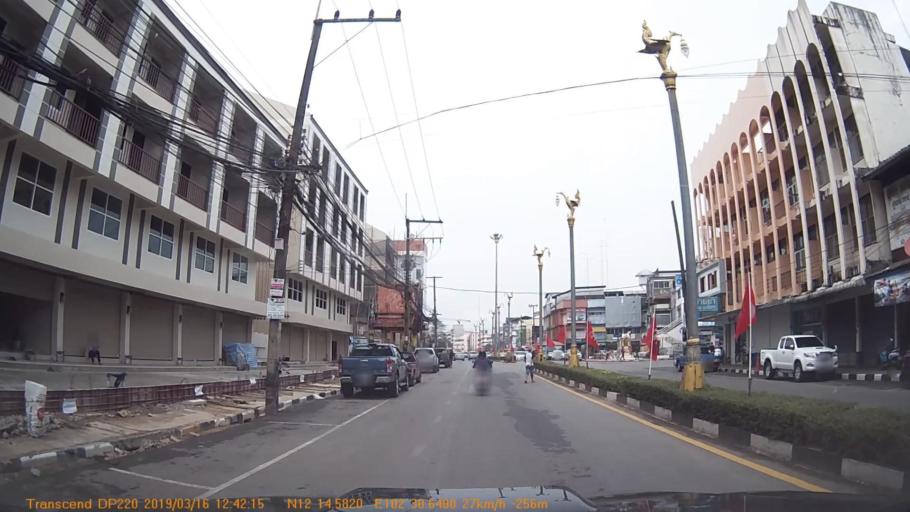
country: TH
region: Trat
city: Trat
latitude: 12.2432
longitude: 102.5106
